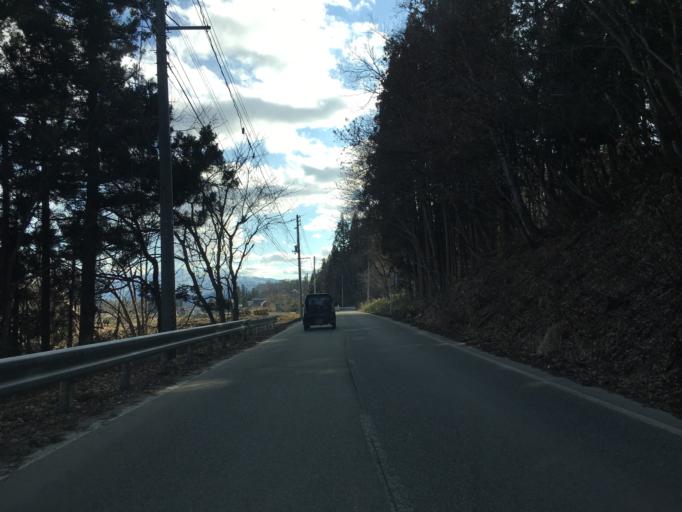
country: JP
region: Yamagata
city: Nagai
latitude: 37.9785
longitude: 139.9997
